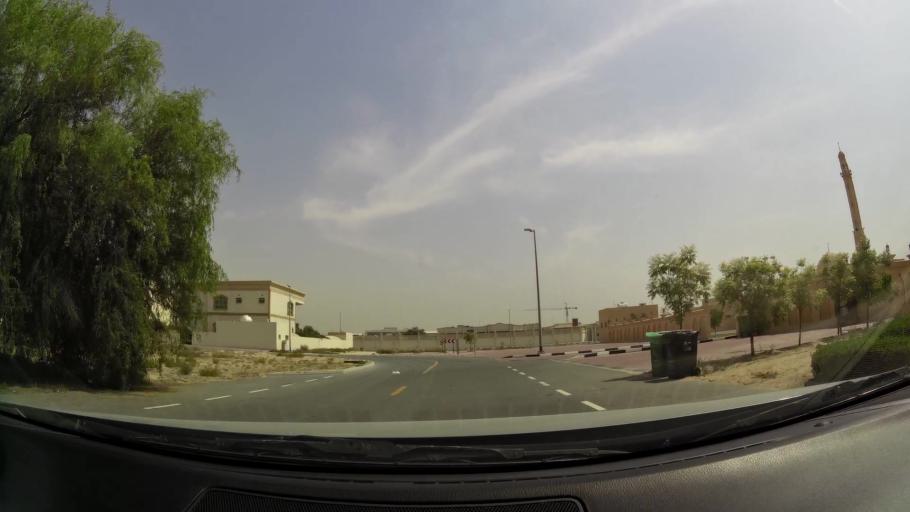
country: AE
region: Ash Shariqah
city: Sharjah
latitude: 25.2390
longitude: 55.4332
